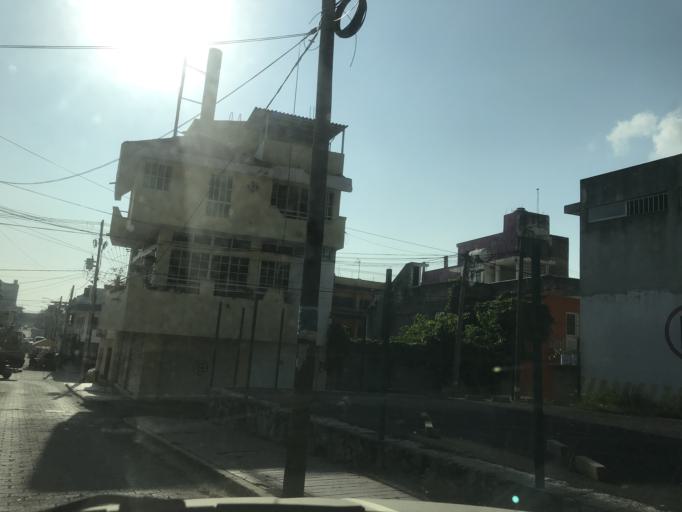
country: MX
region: Colima
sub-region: Manzanillo
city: Manzanillo
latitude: 19.0500
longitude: -104.3190
